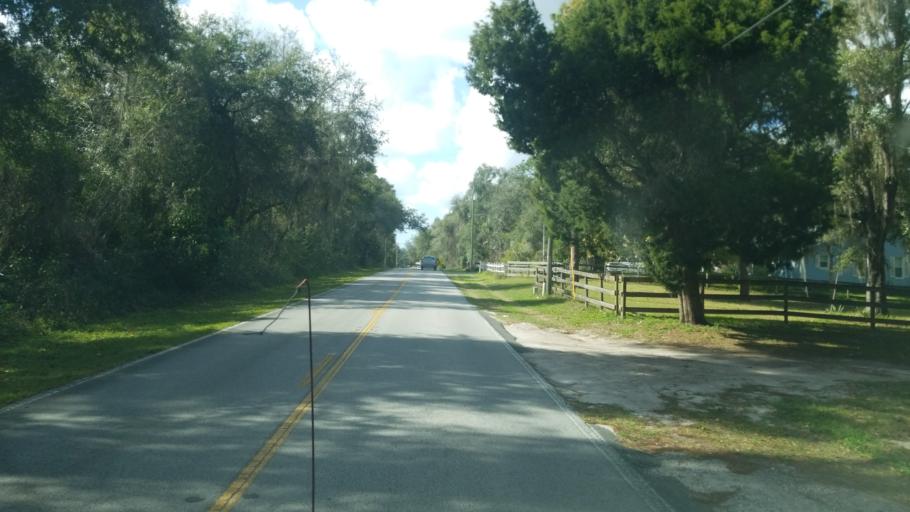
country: US
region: Florida
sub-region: Citrus County
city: Floral City
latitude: 28.7826
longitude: -82.2908
